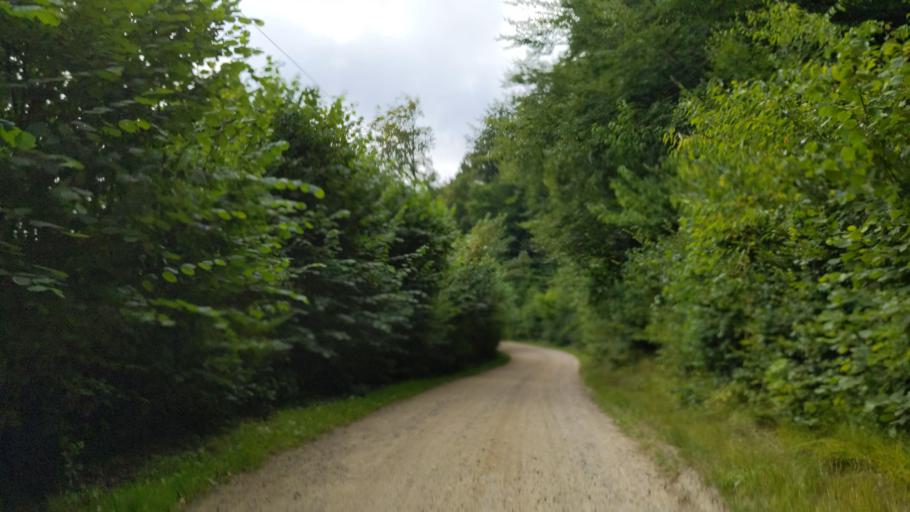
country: DE
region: Schleswig-Holstein
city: Eutin
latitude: 54.1607
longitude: 10.6386
